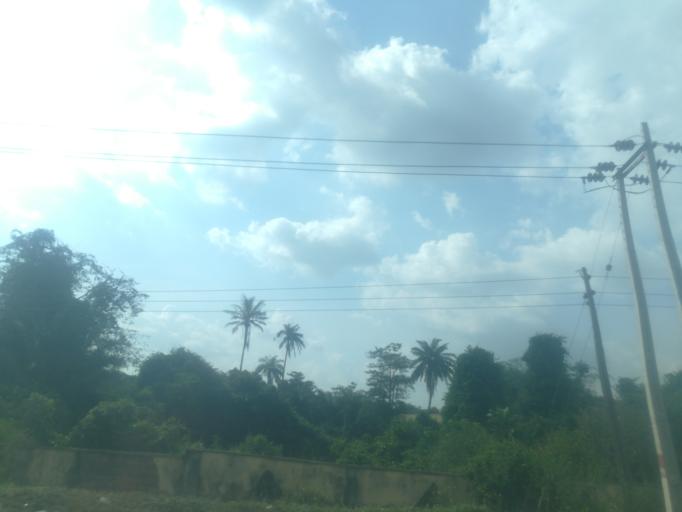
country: NG
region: Ogun
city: Abeokuta
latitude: 7.1255
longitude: 3.2990
